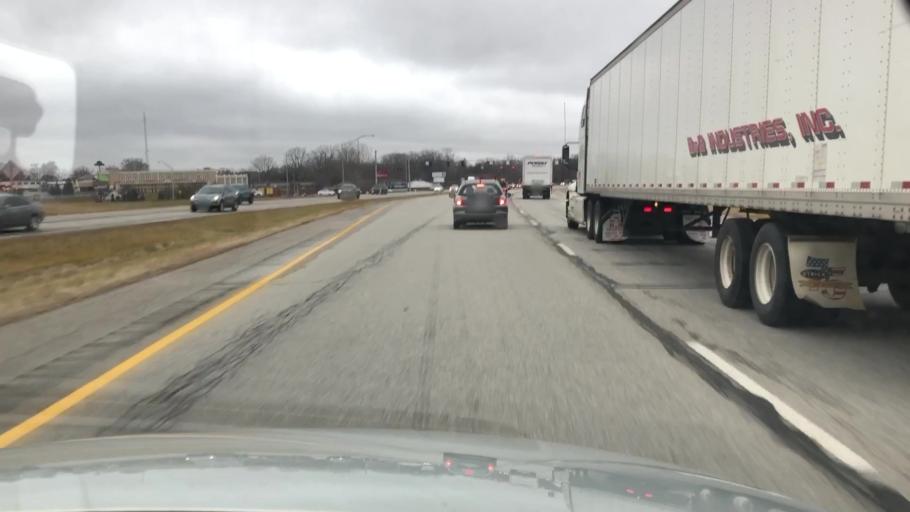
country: US
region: Indiana
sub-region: Kosciusko County
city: Winona Lake
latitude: 41.2376
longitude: -85.8134
